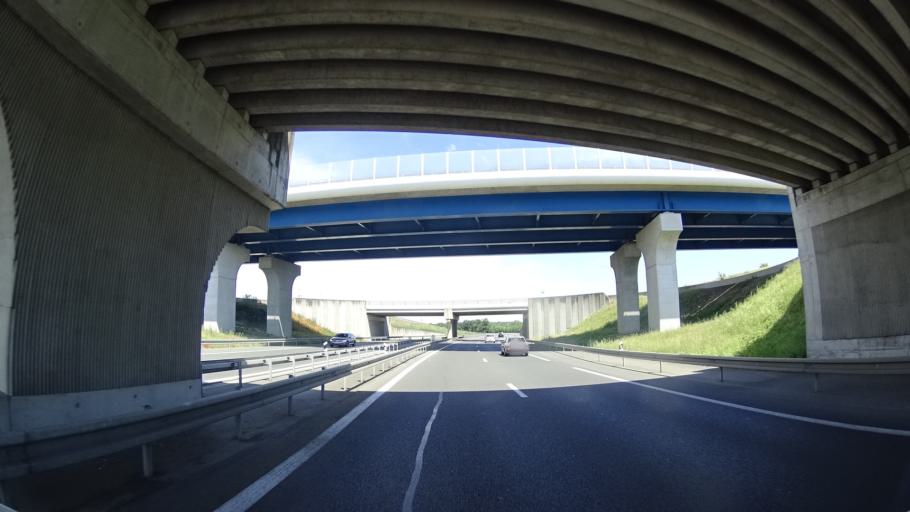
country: FR
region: Pays de la Loire
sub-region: Departement de Maine-et-Loire
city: Beaucouze
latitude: 47.4936
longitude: -0.6227
